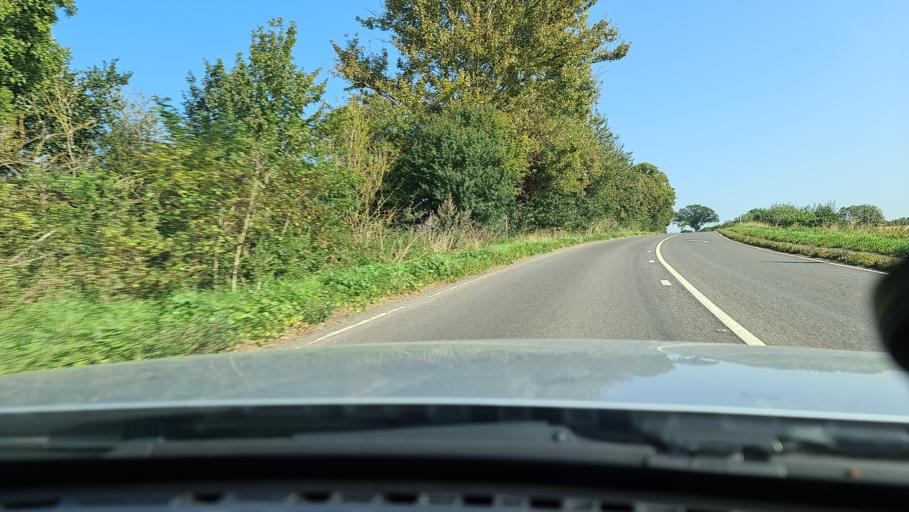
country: GB
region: England
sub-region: Oxfordshire
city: Adderbury
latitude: 52.0029
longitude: -1.3202
